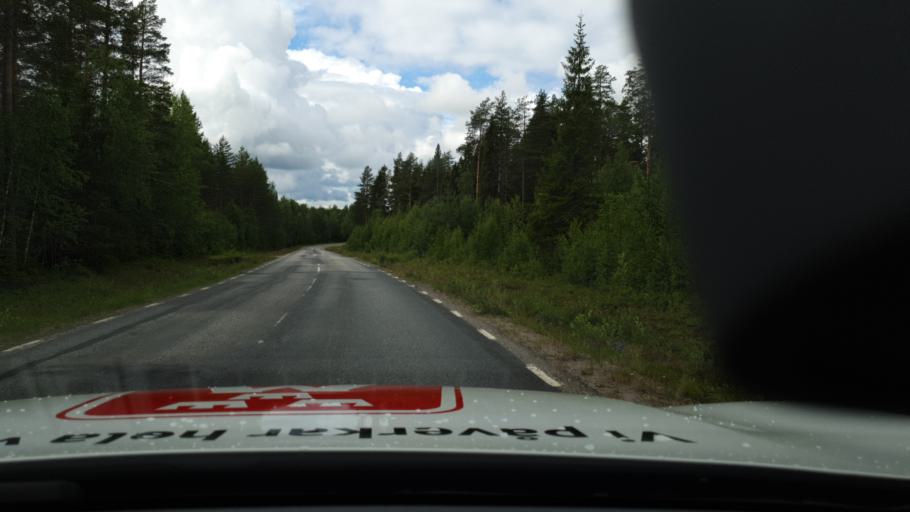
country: SE
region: Norrbotten
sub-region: Bodens Kommun
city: Saevast
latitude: 65.6037
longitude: 21.7342
